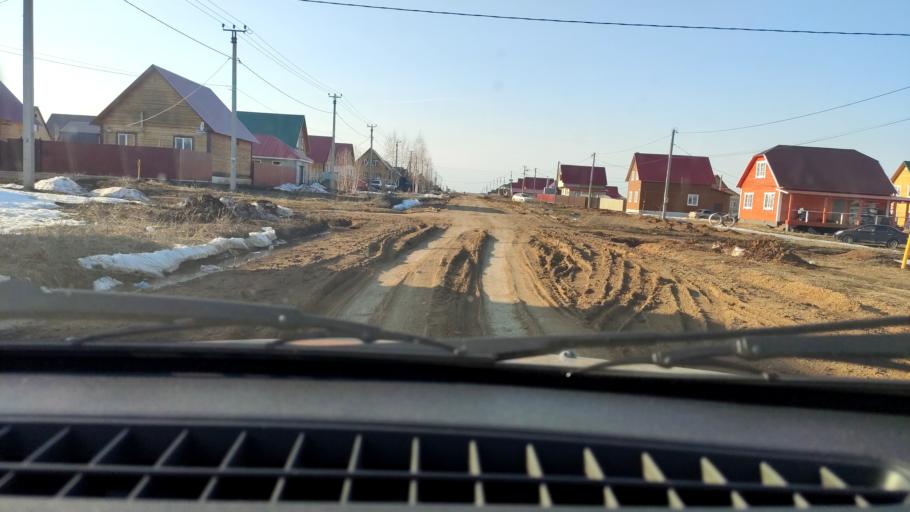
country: RU
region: Bashkortostan
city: Iglino
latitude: 54.8188
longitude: 56.4436
